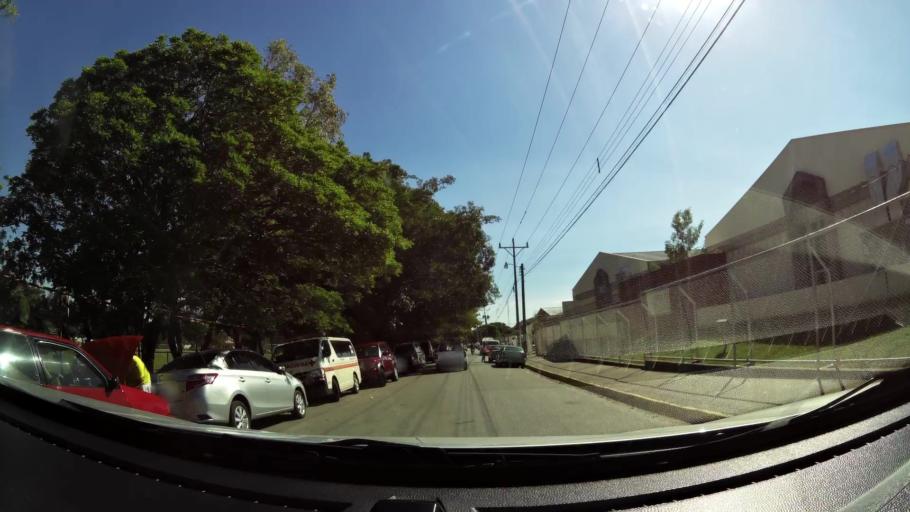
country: CR
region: Guanacaste
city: Liberia
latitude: 10.6392
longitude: -85.4304
